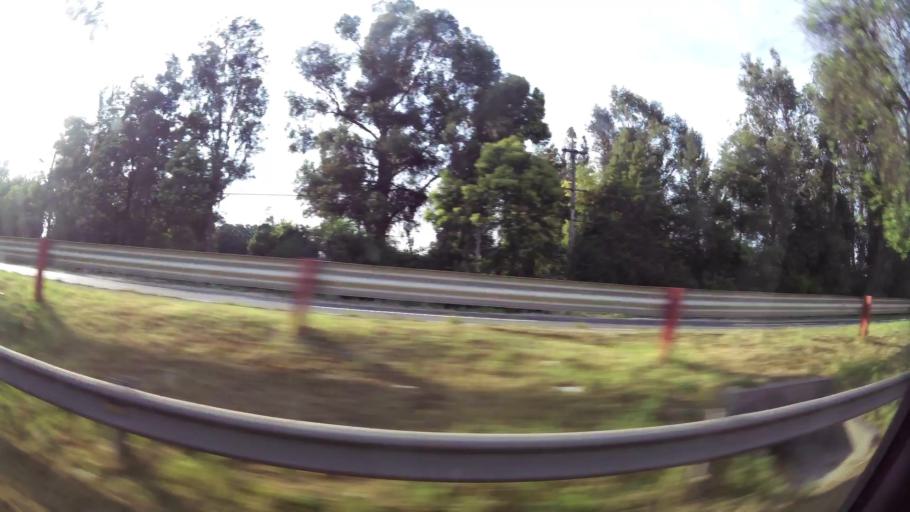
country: CL
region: Santiago Metropolitan
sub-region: Provincia de Talagante
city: Penaflor
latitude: -33.5807
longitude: -70.8283
